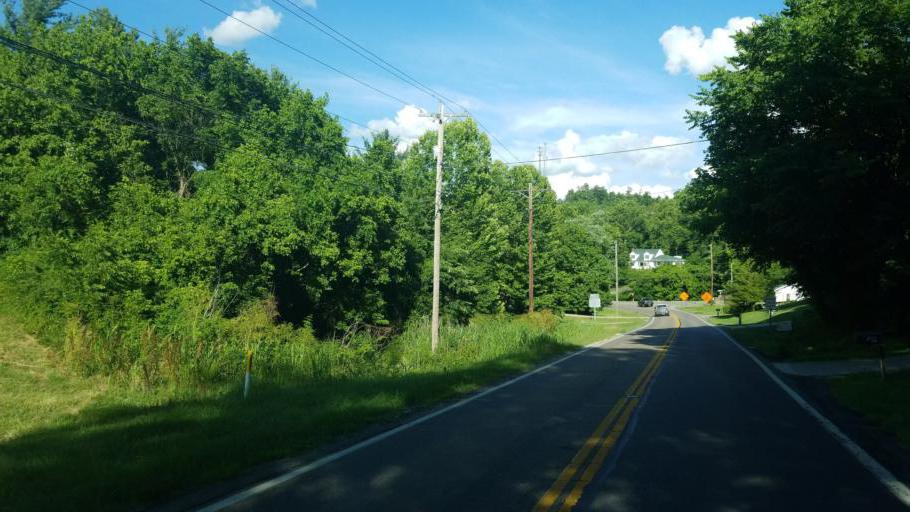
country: US
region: Ohio
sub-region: Gallia County
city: Gallipolis
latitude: 38.8025
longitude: -82.2265
